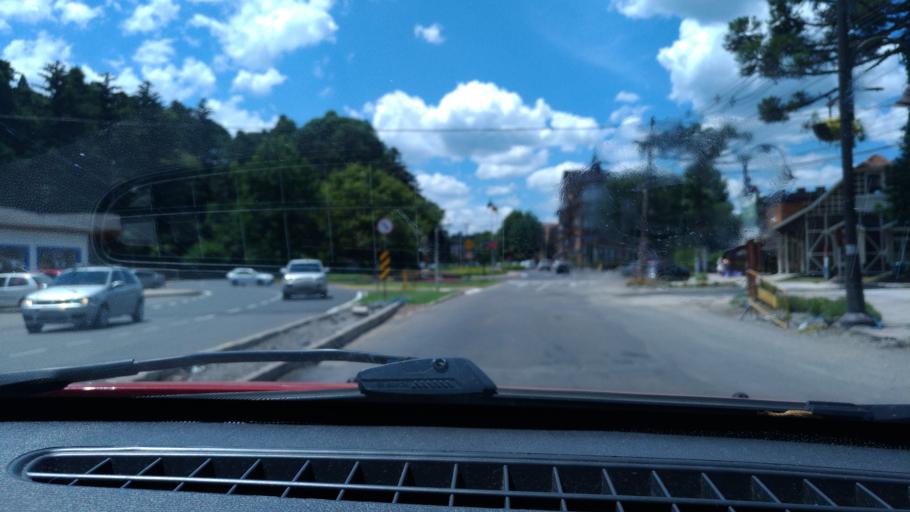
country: BR
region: Rio Grande do Sul
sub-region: Canela
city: Canela
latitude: -29.3862
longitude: -50.8737
